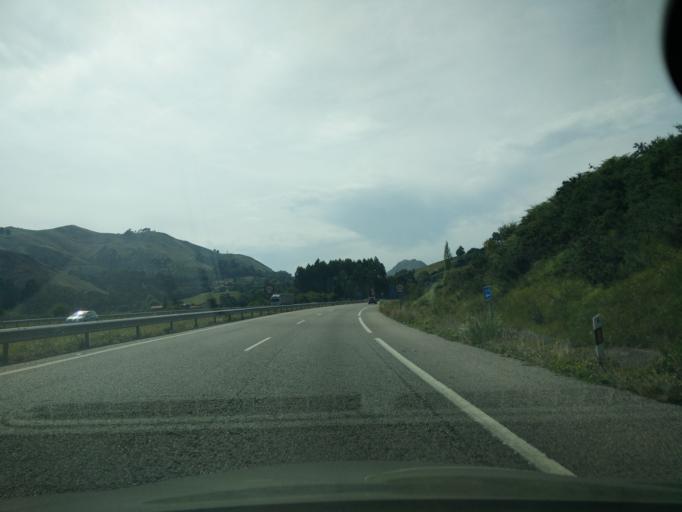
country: ES
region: Asturias
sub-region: Province of Asturias
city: Ribadesella
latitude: 43.4405
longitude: -5.0849
